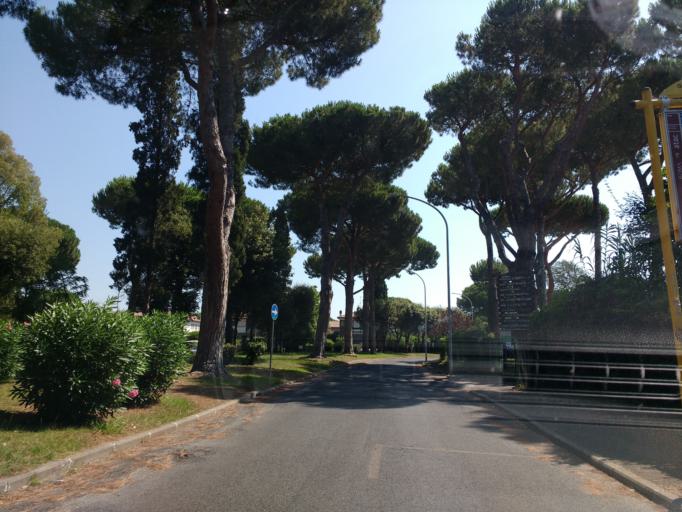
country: IT
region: Latium
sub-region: Citta metropolitana di Roma Capitale
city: Acilia-Castel Fusano-Ostia Antica
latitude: 41.7581
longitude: 12.3585
